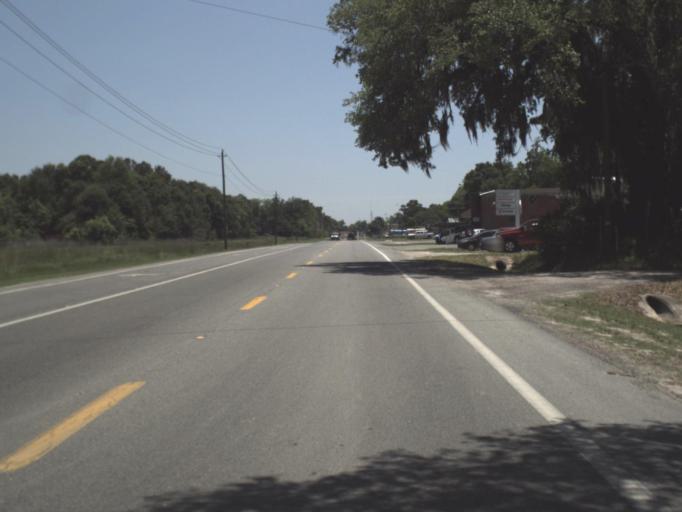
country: US
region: Florida
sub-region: Suwannee County
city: Live Oak
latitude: 30.3034
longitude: -83.0003
